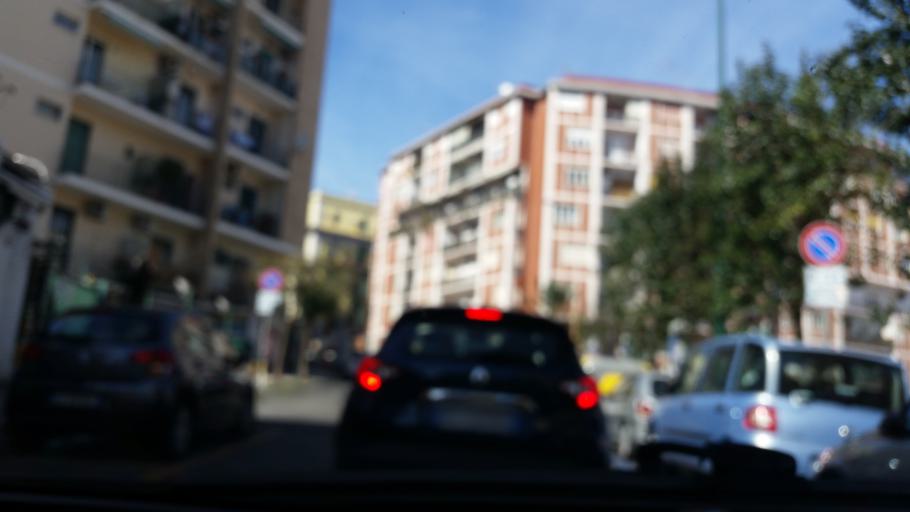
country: IT
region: Campania
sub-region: Provincia di Napoli
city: Napoli
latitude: 40.8532
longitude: 14.2335
